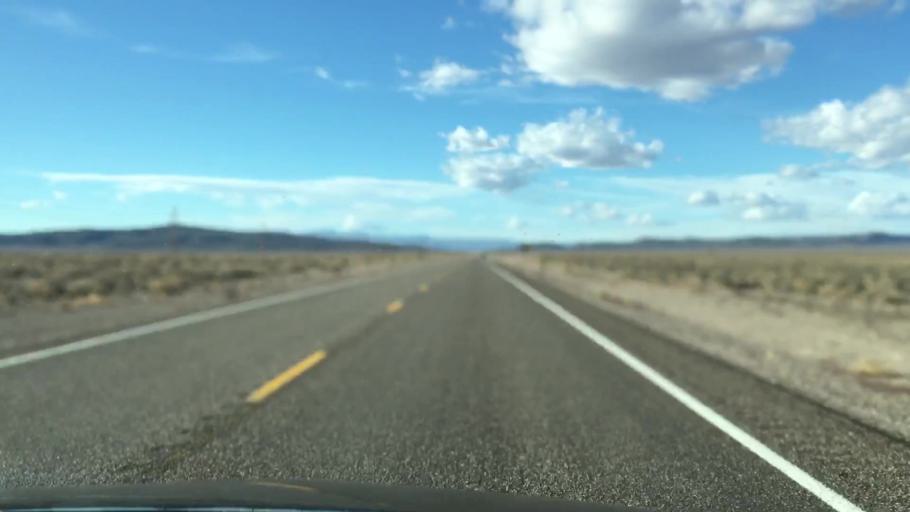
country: US
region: Nevada
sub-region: Nye County
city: Beatty
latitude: 37.1353
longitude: -116.8500
